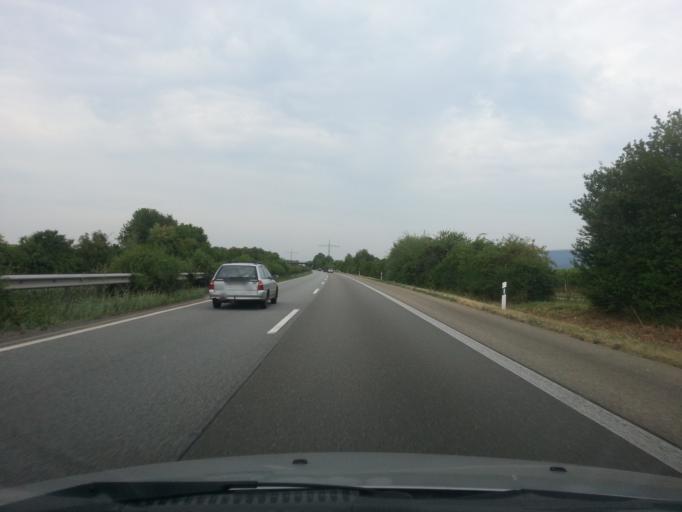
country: DE
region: Rheinland-Pfalz
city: Kirrweiler
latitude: 49.3126
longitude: 8.1608
